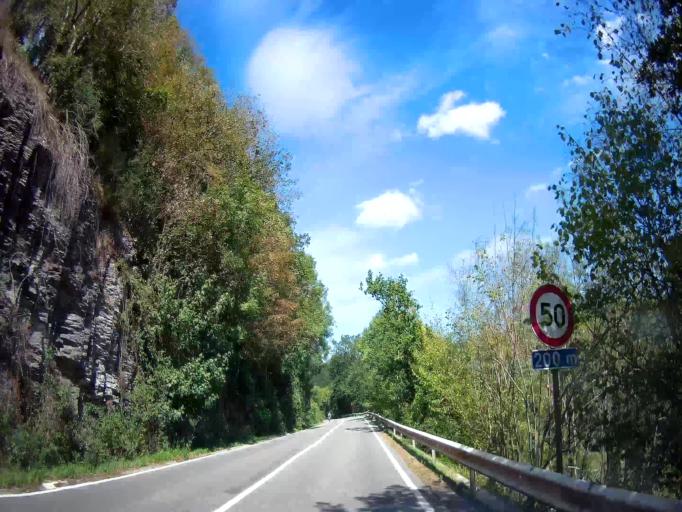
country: BE
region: Wallonia
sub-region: Province du Luxembourg
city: Rendeux
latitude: 50.2055
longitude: 5.5362
